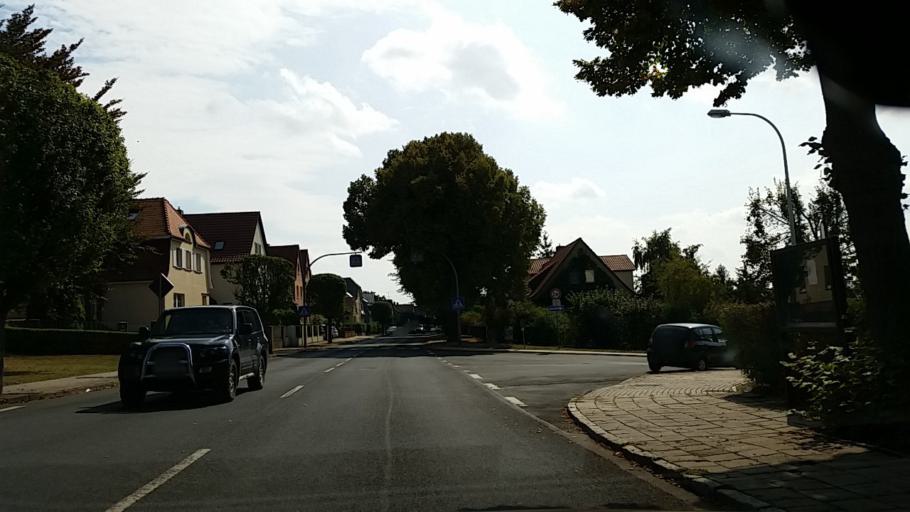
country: DE
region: Thuringia
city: Artern
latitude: 51.3700
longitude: 11.2900
